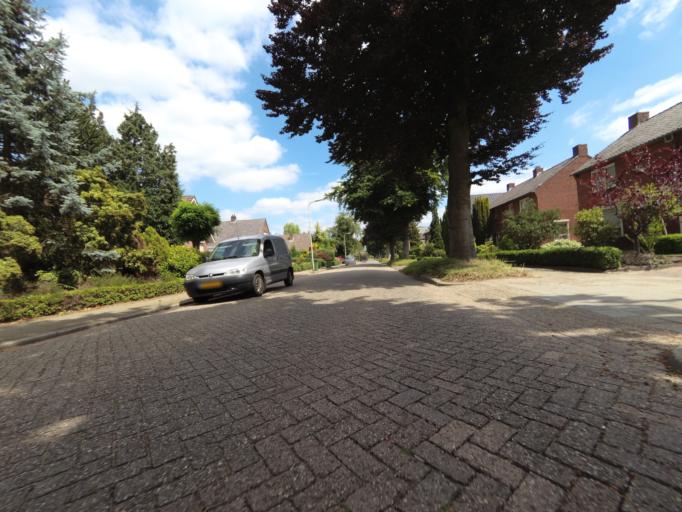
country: NL
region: Overijssel
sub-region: Gemeente Twenterand
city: Den Ham
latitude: 52.3526
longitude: 6.4729
